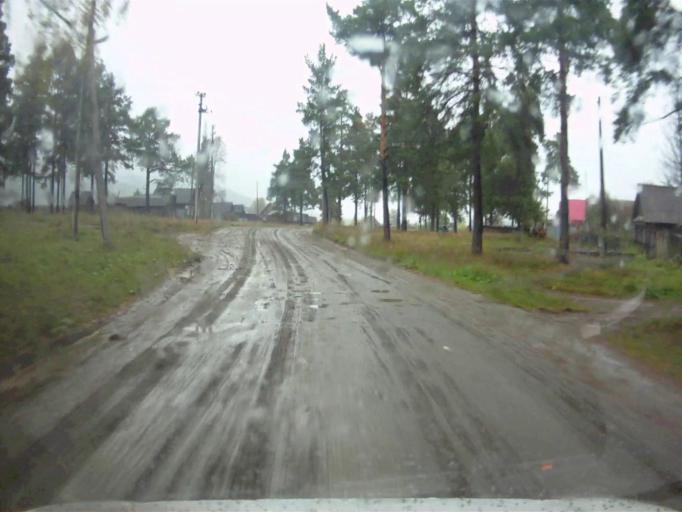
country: RU
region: Chelyabinsk
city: Kyshtym
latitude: 55.9003
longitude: 60.4659
